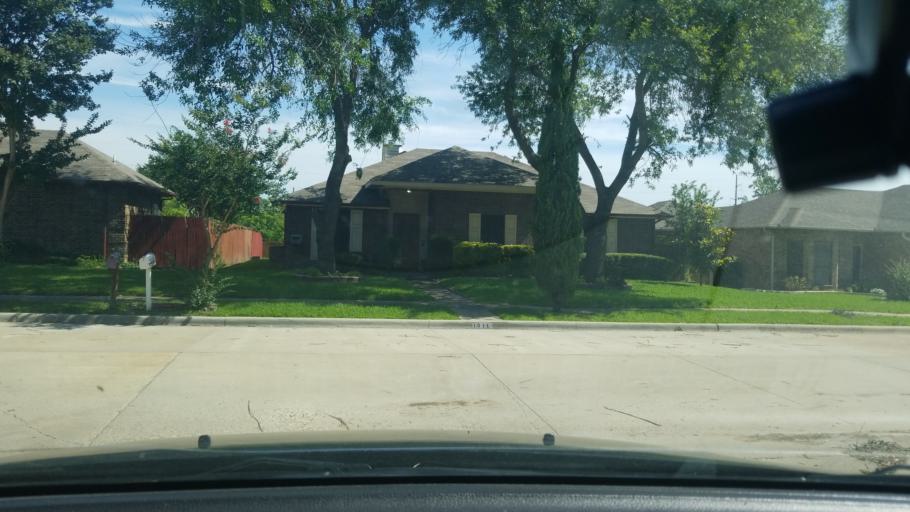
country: US
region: Texas
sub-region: Dallas County
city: Mesquite
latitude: 32.7738
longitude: -96.5853
